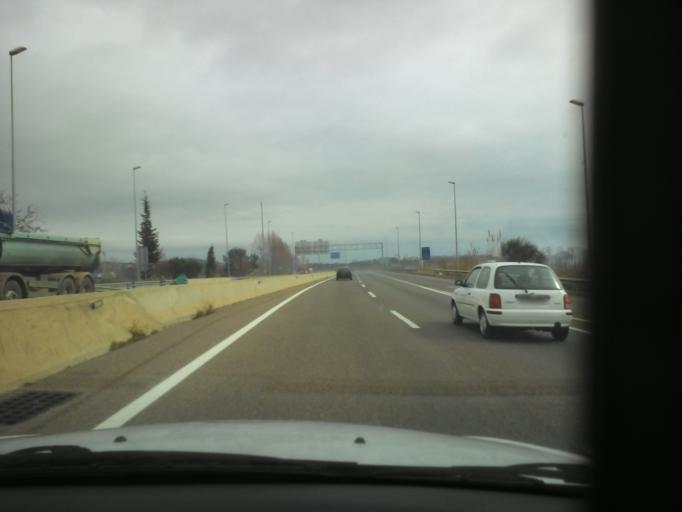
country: ES
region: Catalonia
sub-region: Provincia de Girona
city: Sant Feliu de Guixols
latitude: 41.8090
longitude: 3.0363
